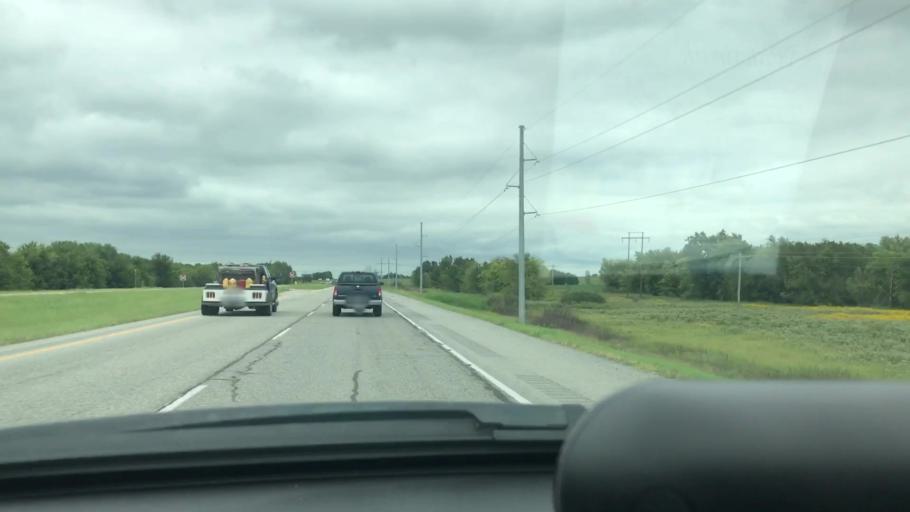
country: US
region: Oklahoma
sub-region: Wagoner County
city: Wagoner
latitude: 36.0013
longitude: -95.3685
